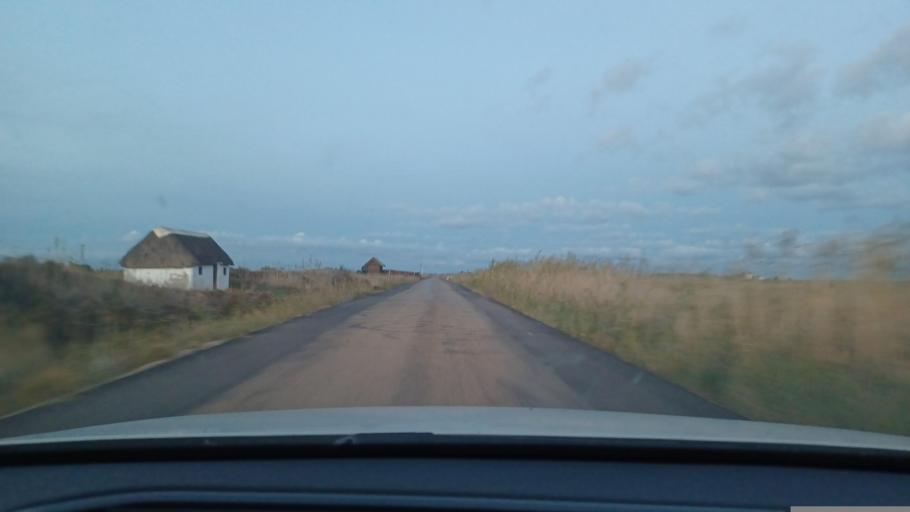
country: ES
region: Catalonia
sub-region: Provincia de Tarragona
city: Deltebre
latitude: 40.6450
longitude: 0.7557
